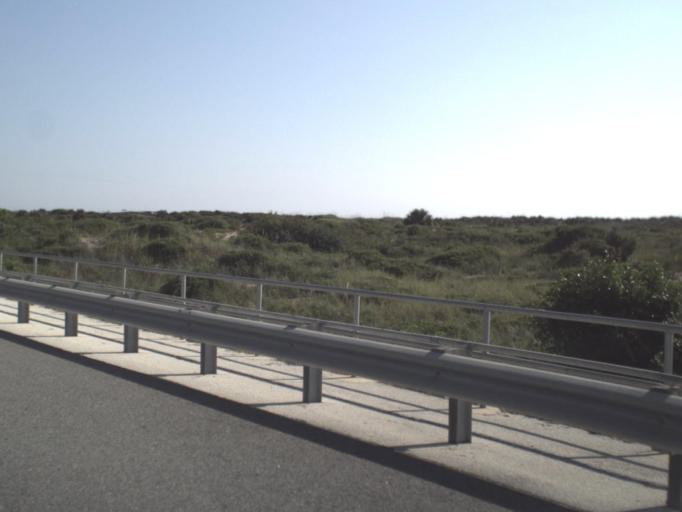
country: US
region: Florida
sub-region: Saint Johns County
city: Butler Beach
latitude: 29.7107
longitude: -81.2296
